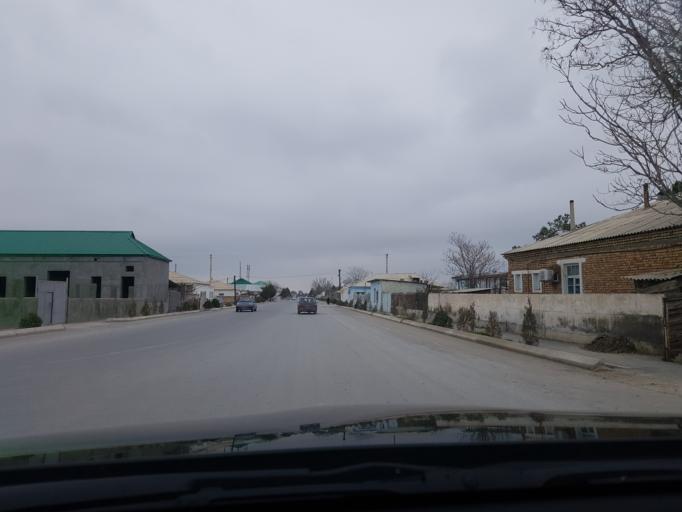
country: TM
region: Ahal
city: Abadan
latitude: 38.1503
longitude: 57.9573
